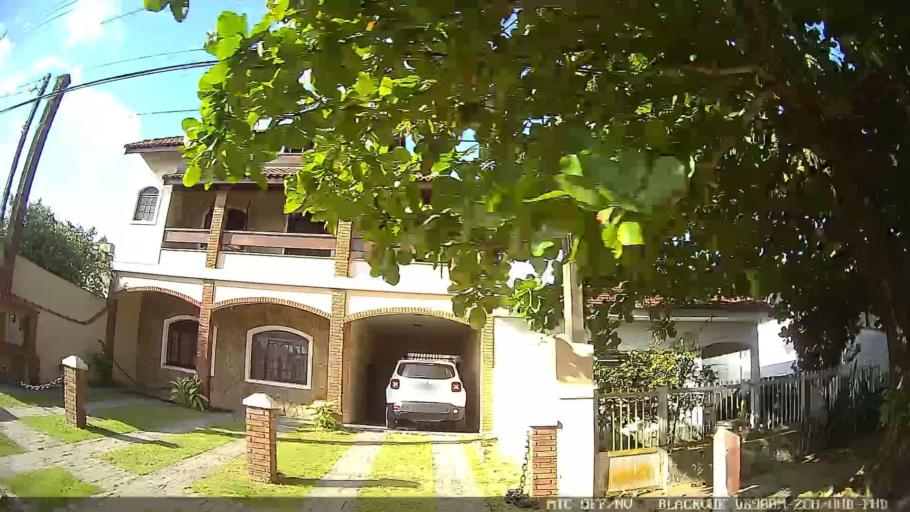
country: BR
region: Sao Paulo
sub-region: Peruibe
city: Peruibe
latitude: -24.2928
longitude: -46.9620
